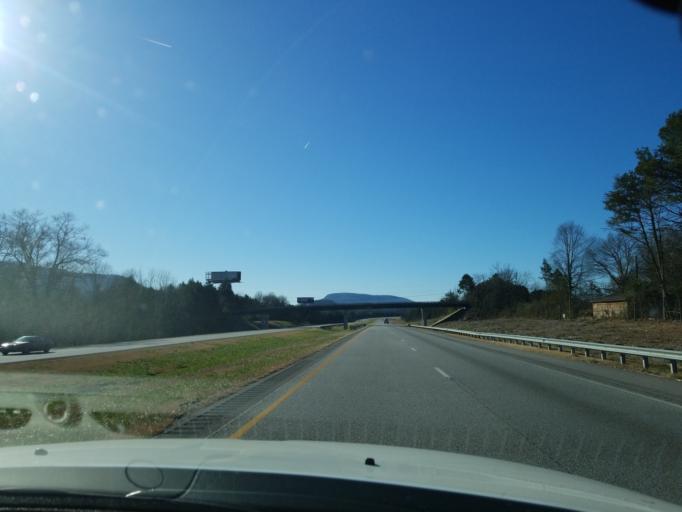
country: US
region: Georgia
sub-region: Dade County
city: Trenton
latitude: 34.8332
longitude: -85.5351
